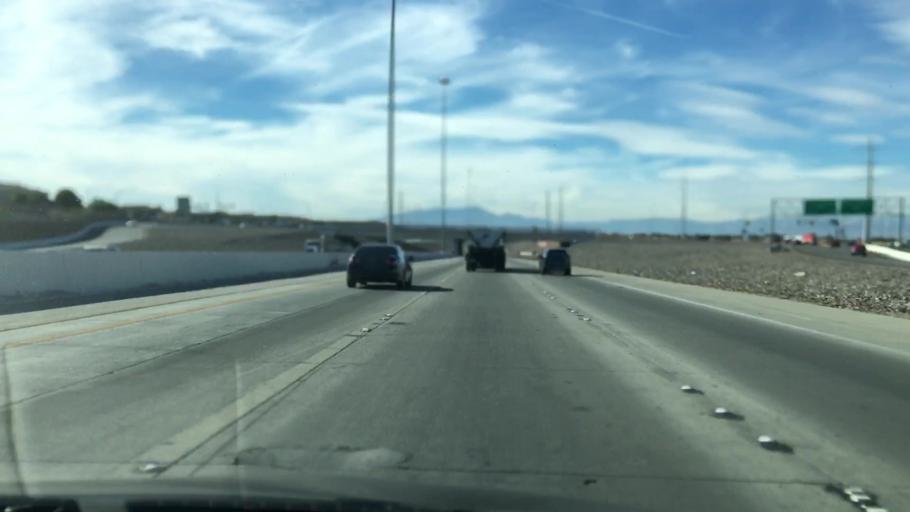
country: US
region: Nevada
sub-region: Clark County
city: Whitney
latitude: 36.0299
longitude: -115.0441
